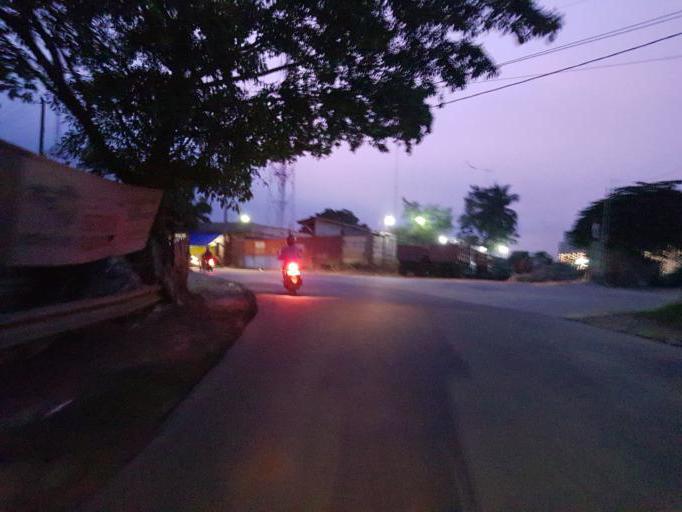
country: ID
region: West Java
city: Serpong
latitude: -6.3108
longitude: 106.6575
